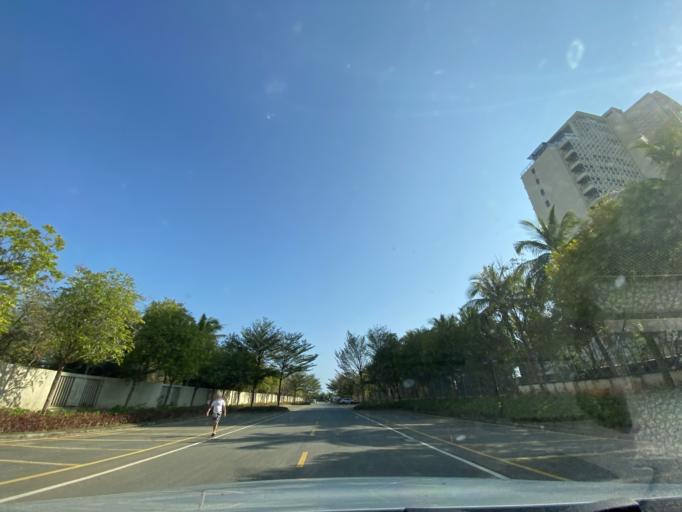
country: CN
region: Hainan
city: Yingzhou
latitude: 18.4158
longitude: 109.8970
